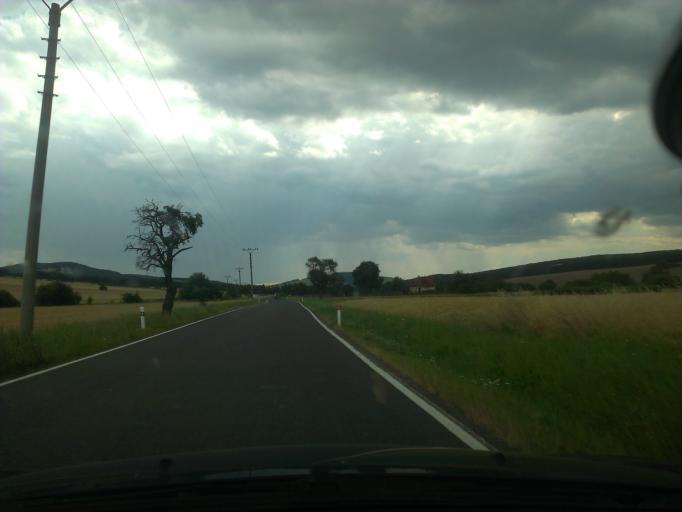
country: CZ
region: South Moravian
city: Velka nad Velickou
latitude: 48.8559
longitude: 17.5227
